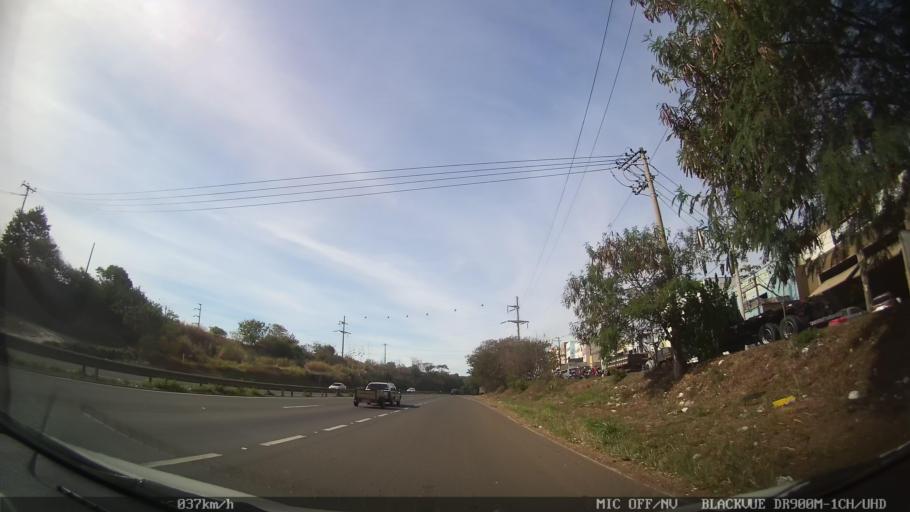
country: BR
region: Sao Paulo
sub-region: Piracicaba
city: Piracicaba
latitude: -22.6871
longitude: -47.6704
